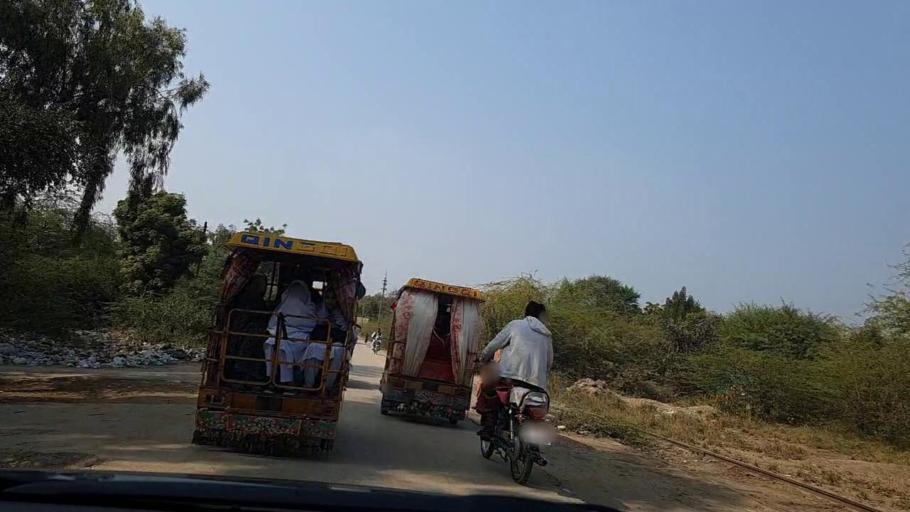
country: PK
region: Sindh
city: Sakrand
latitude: 26.1413
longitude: 68.2757
